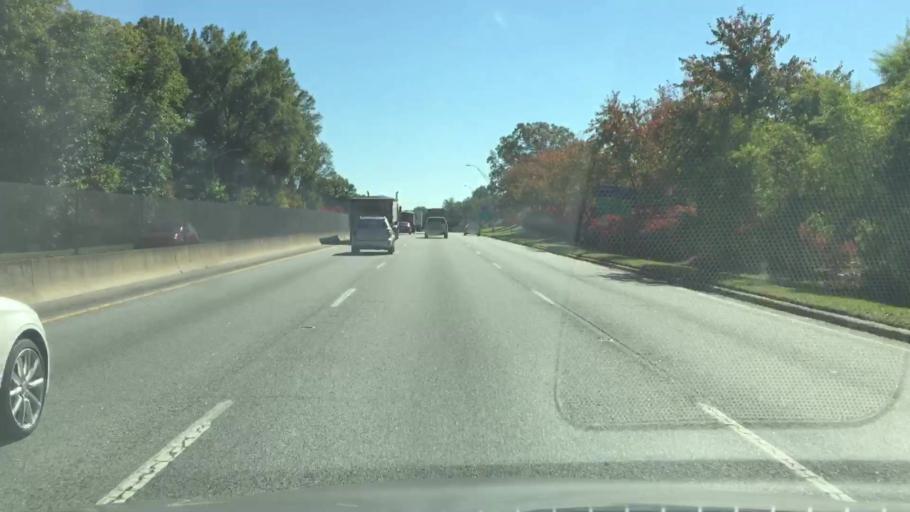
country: US
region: North Carolina
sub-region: Guilford County
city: Greensboro
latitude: 36.0768
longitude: -79.7669
